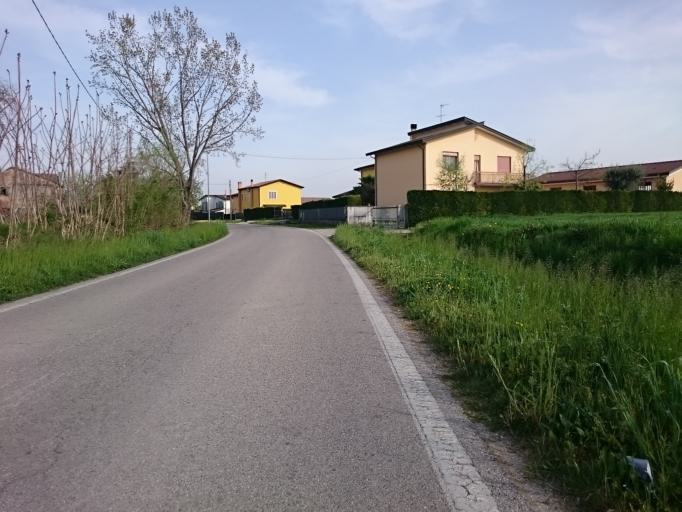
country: IT
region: Veneto
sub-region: Provincia di Padova
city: Masera di Padova
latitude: 45.3105
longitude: 11.8713
